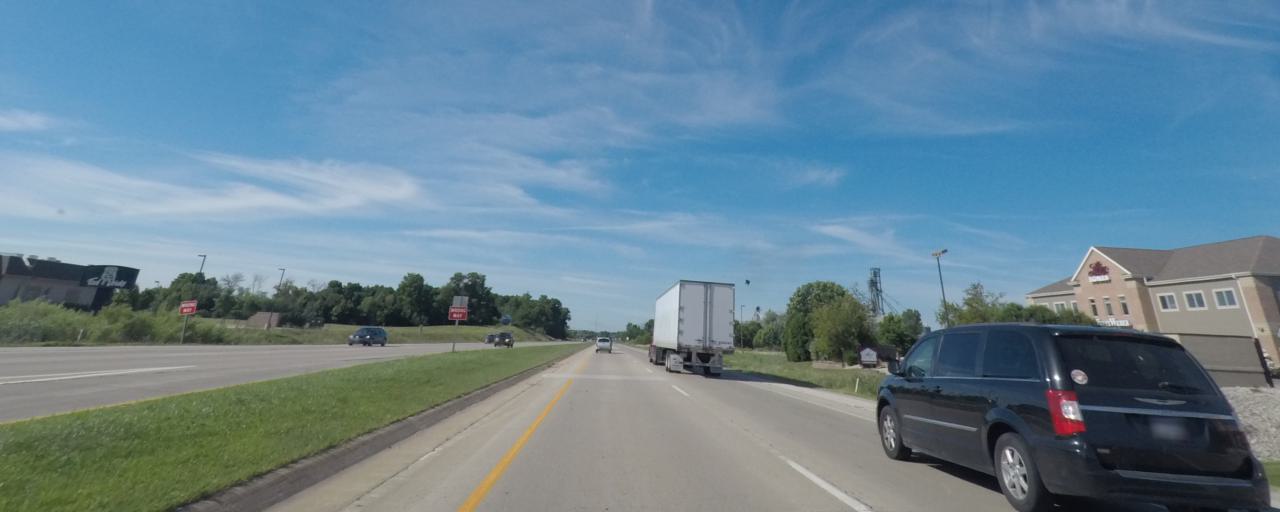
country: US
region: Wisconsin
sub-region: Jefferson County
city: Johnson Creek
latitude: 43.0821
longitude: -88.7638
